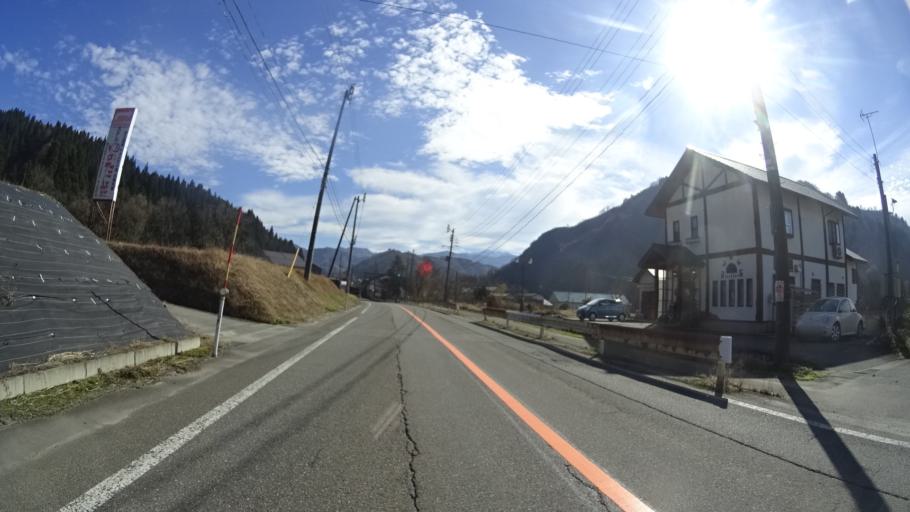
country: JP
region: Niigata
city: Muikamachi
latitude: 37.2112
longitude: 139.0562
